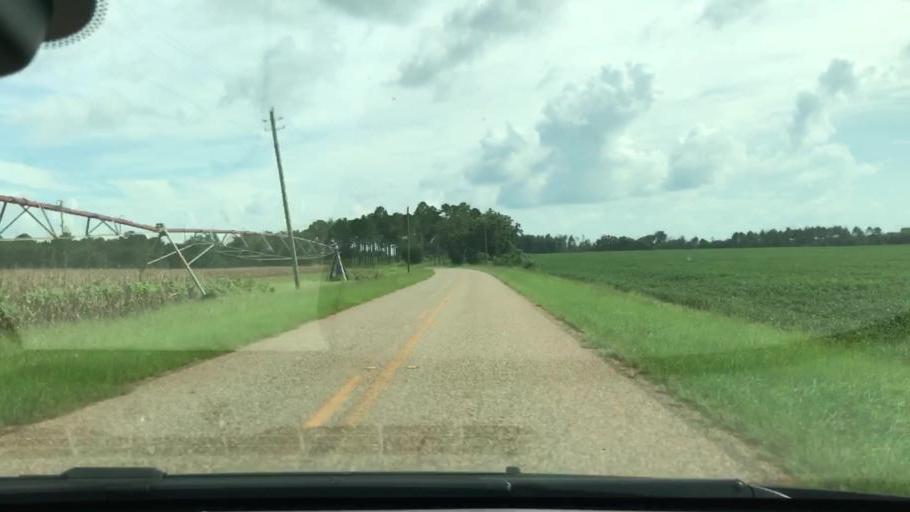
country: US
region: Georgia
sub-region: Clay County
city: Fort Gaines
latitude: 31.5191
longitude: -84.9546
